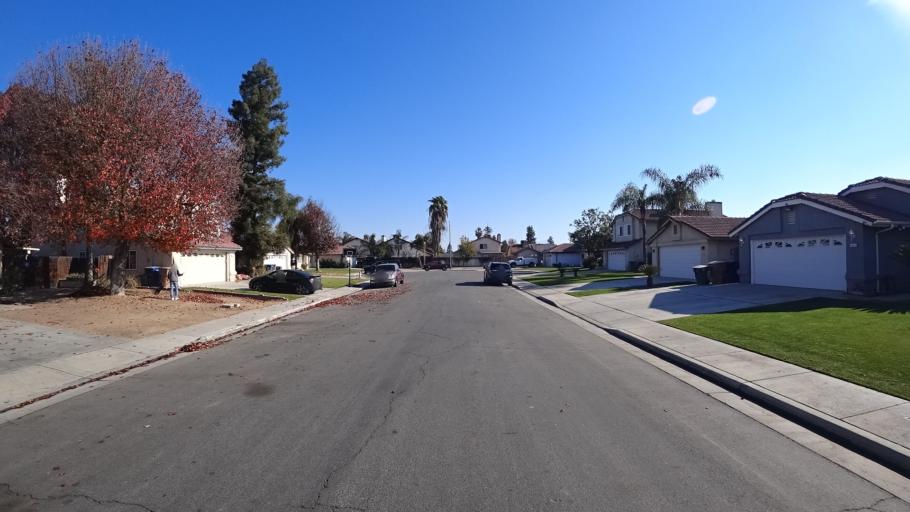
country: US
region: California
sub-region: Kern County
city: Greenfield
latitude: 35.2938
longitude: -119.0535
